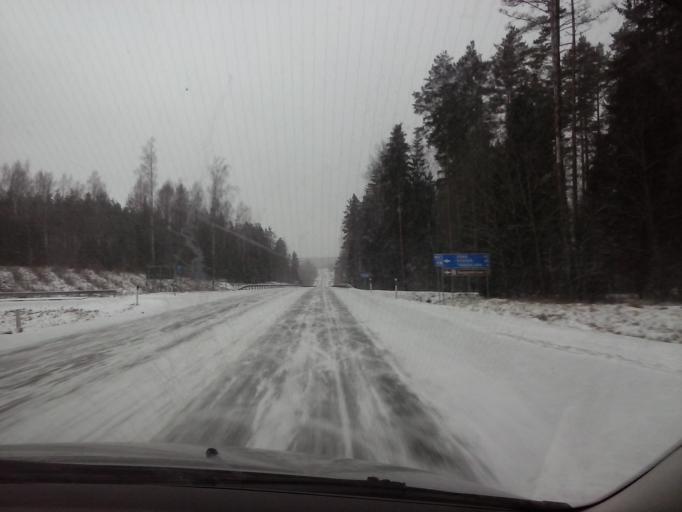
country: EE
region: Valgamaa
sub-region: Valga linn
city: Valga
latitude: 57.8562
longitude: 26.1379
